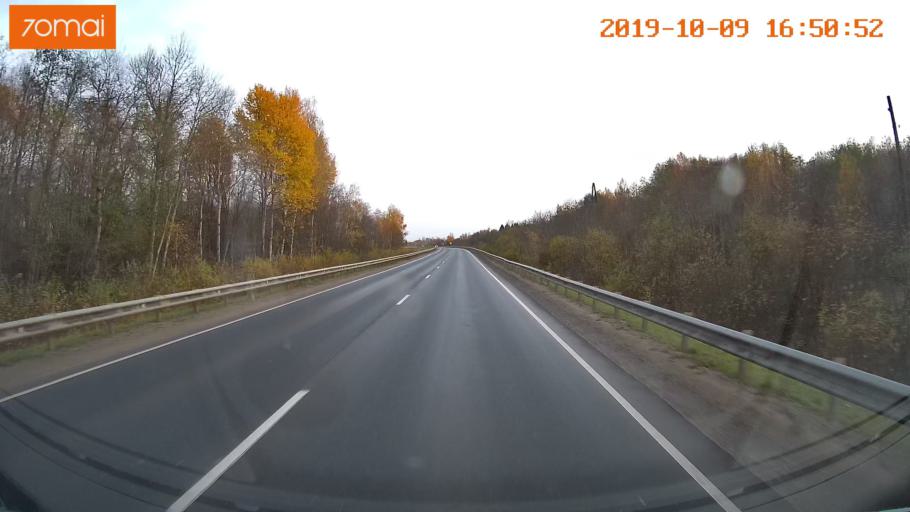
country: RU
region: Ivanovo
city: Privolzhsk
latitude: 57.3949
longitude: 41.2144
